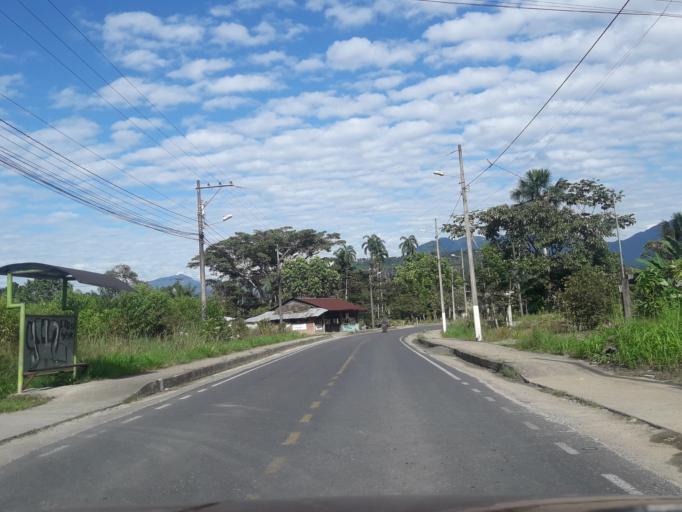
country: EC
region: Napo
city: Tena
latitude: -0.9867
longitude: -77.8341
